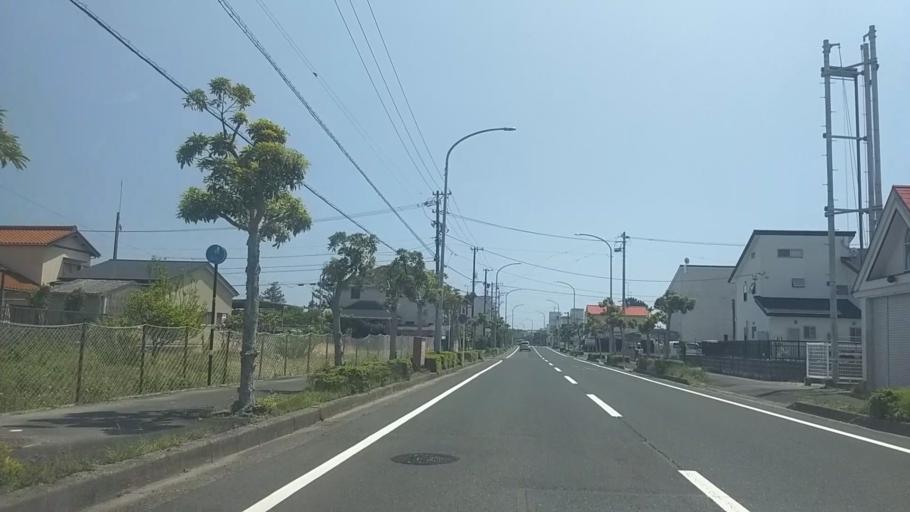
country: JP
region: Shizuoka
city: Kosai-shi
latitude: 34.6879
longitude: 137.5696
